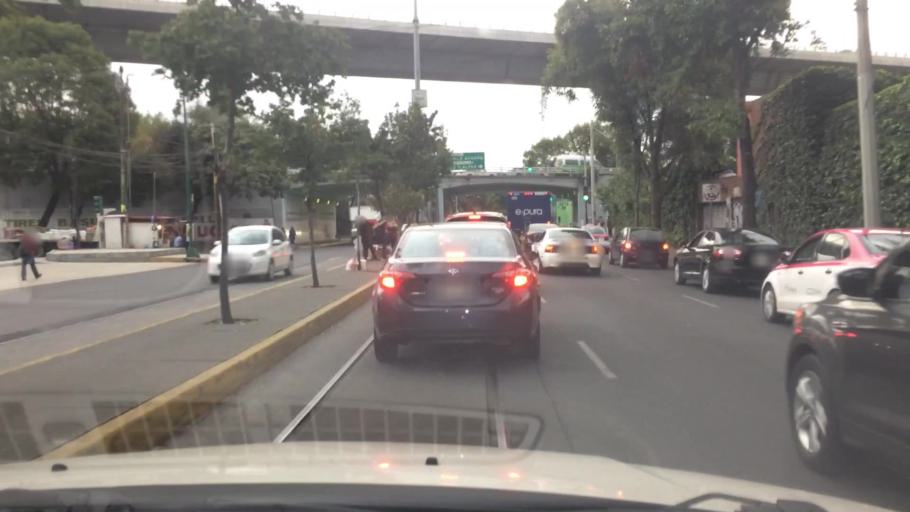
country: MX
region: Mexico City
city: Tlalpan
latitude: 19.2966
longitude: -99.1575
